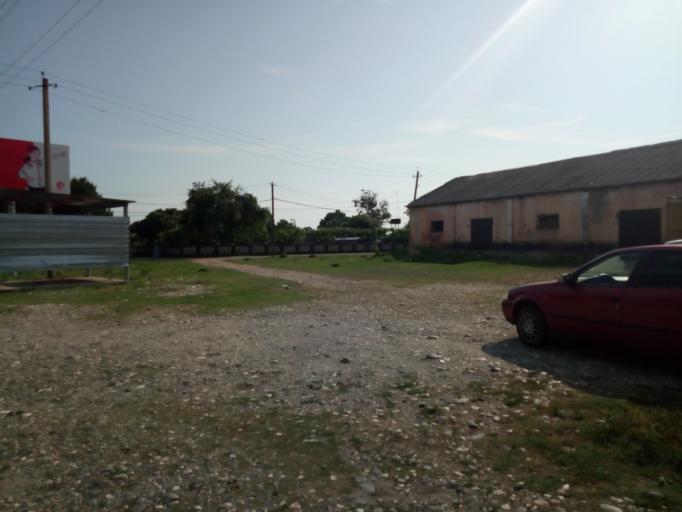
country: GE
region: Abkhazia
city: Och'amch'ire
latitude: 42.8488
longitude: 41.3779
